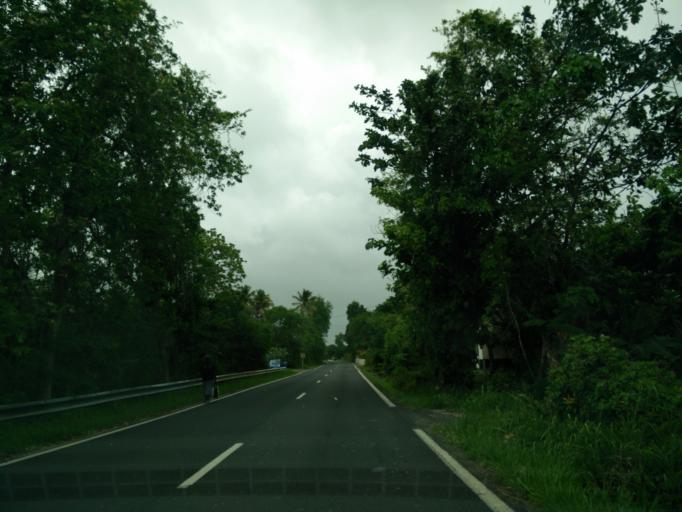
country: GP
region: Guadeloupe
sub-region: Guadeloupe
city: Grand-Bourg
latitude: 15.9071
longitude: -61.2649
